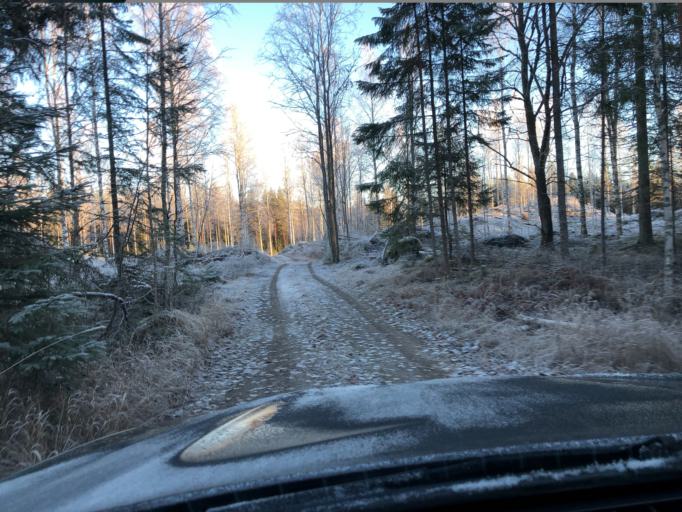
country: FI
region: Pirkanmaa
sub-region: Etelae-Pirkanmaa
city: Akaa
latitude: 60.9608
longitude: 23.9375
